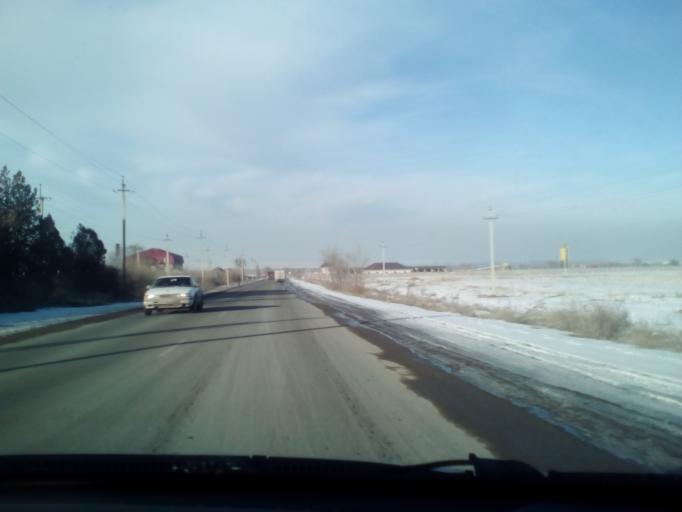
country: KZ
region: Almaty Oblysy
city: Burunday
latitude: 43.1996
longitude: 76.4149
